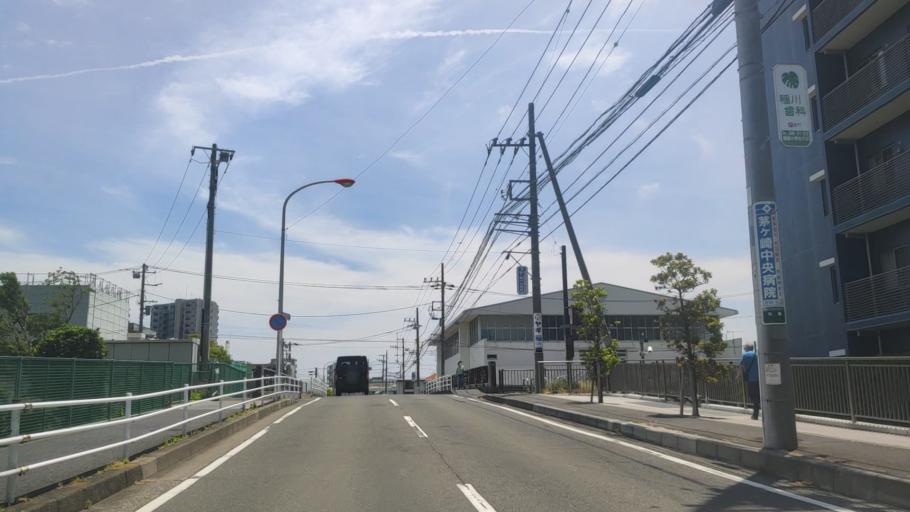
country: JP
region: Kanagawa
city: Chigasaki
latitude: 35.3339
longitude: 139.3996
